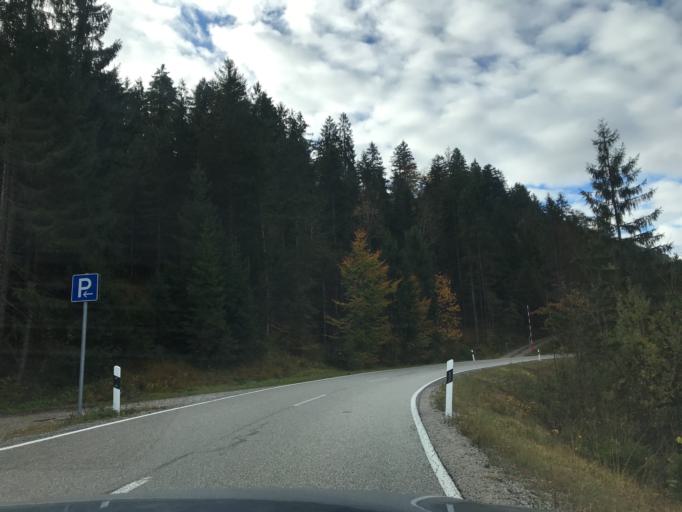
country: DE
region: Bavaria
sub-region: Upper Bavaria
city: Jachenau
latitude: 47.5340
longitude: 11.4416
